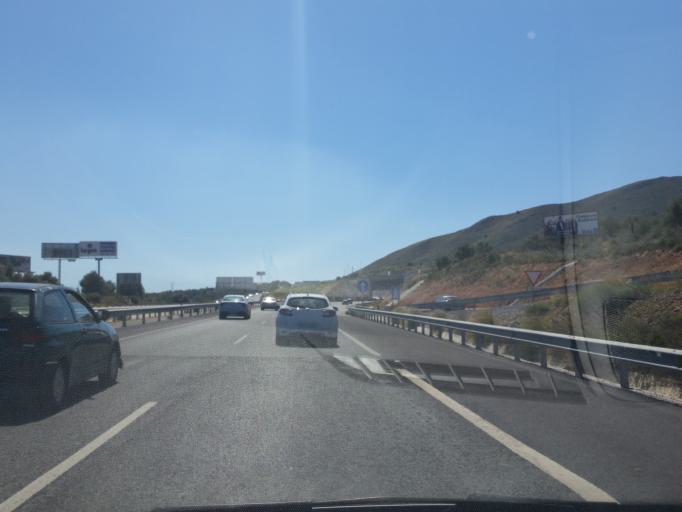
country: ES
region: Andalusia
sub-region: Provincia de Malaga
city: Torremolinos
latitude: 36.6360
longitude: -4.5102
